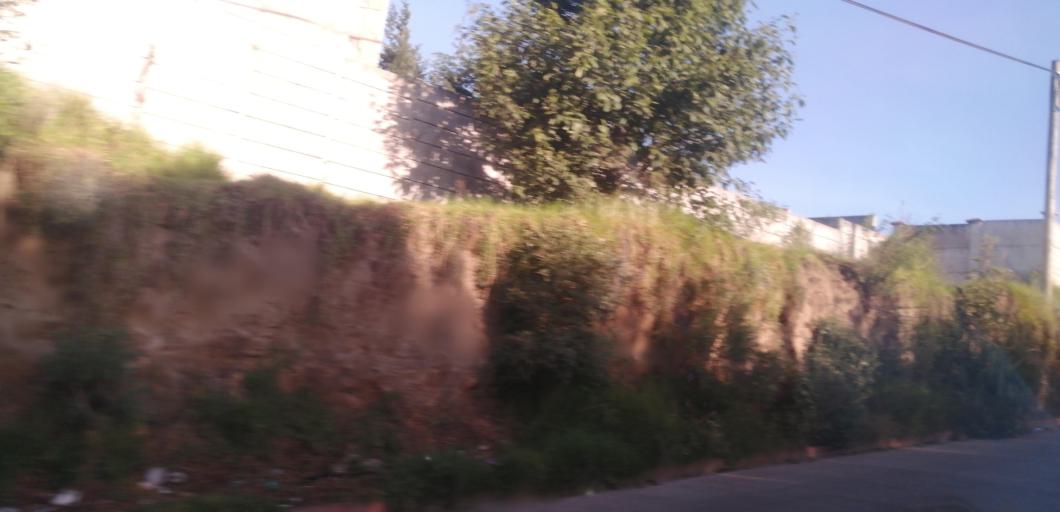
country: GT
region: Quetzaltenango
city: Olintepeque
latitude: 14.8679
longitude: -91.5392
